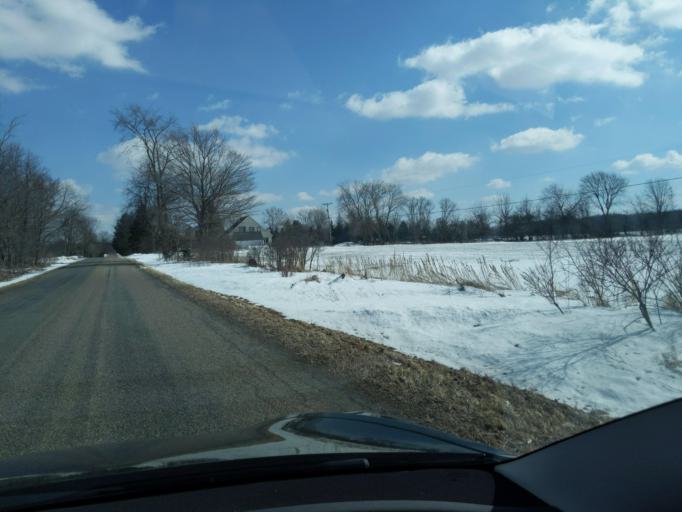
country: US
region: Michigan
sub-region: Ingham County
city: Mason
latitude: 42.6109
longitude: -84.3751
